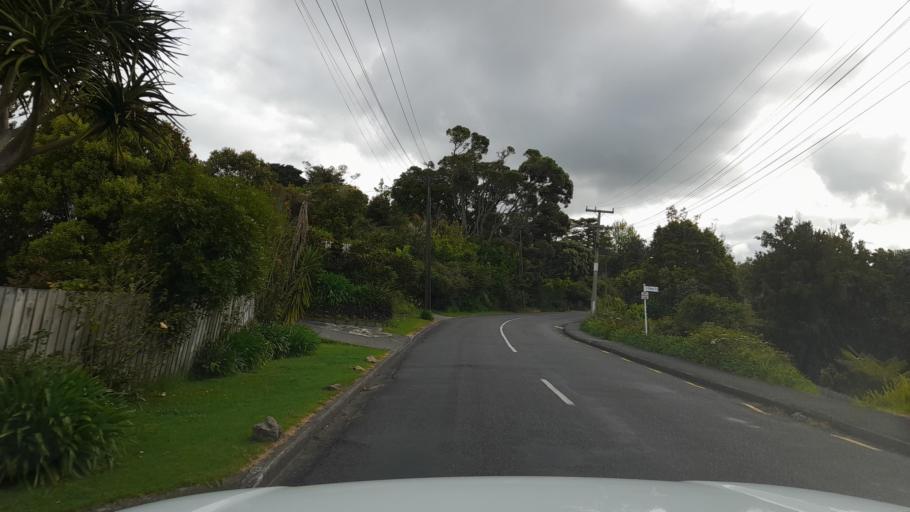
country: NZ
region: Northland
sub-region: Whangarei
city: Whangarei
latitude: -35.7392
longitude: 174.3212
